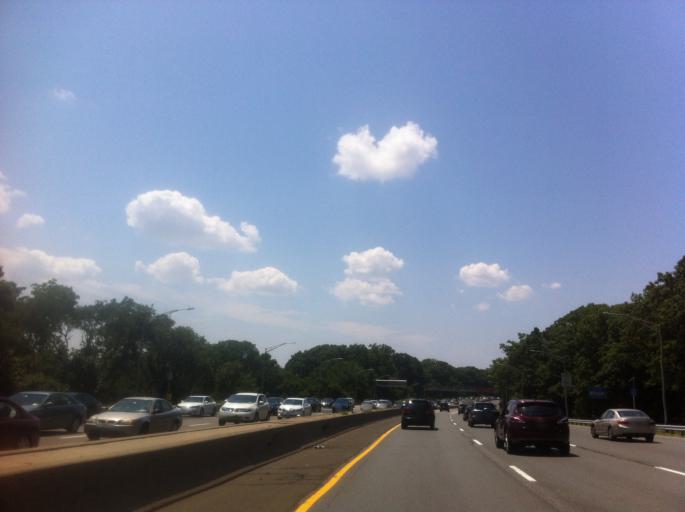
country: US
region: New York
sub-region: Nassau County
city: Lake Success
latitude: 40.7523
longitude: -73.7259
